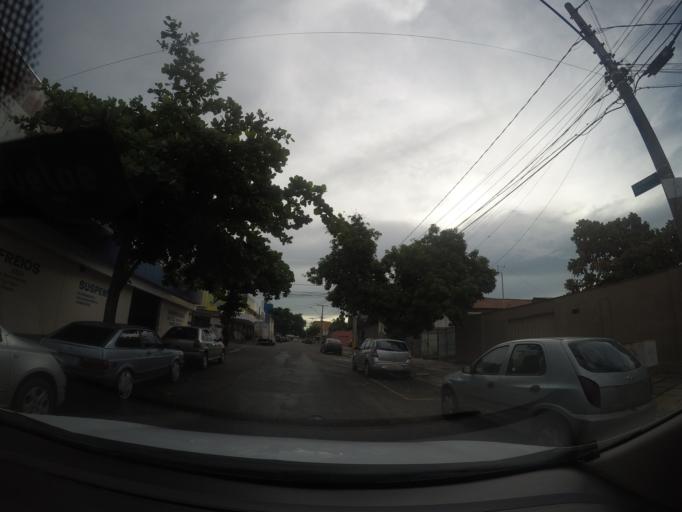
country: BR
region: Goias
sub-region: Goiania
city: Goiania
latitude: -16.6737
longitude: -49.2791
